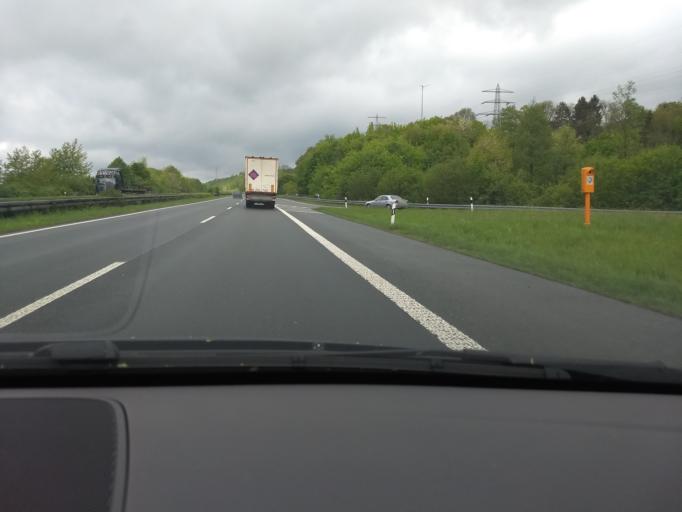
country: DE
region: North Rhine-Westphalia
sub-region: Regierungsbezirk Arnsberg
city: Arnsberg
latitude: 51.4045
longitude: 8.0866
